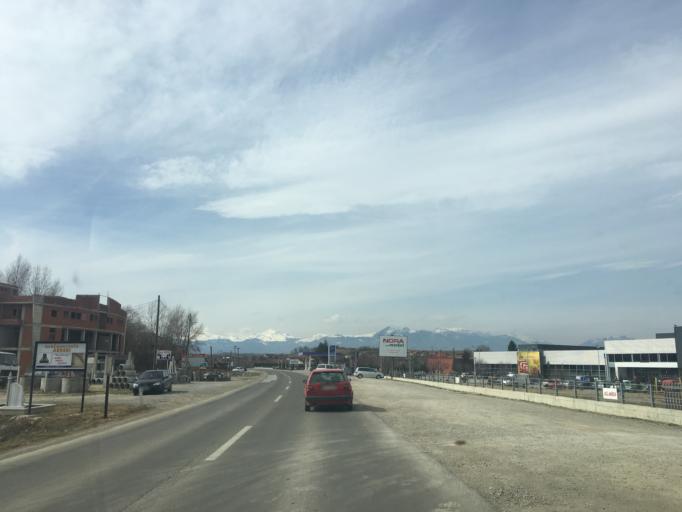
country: XK
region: Pec
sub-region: Komuna e Klines
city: Klina
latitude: 42.5930
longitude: 20.5711
